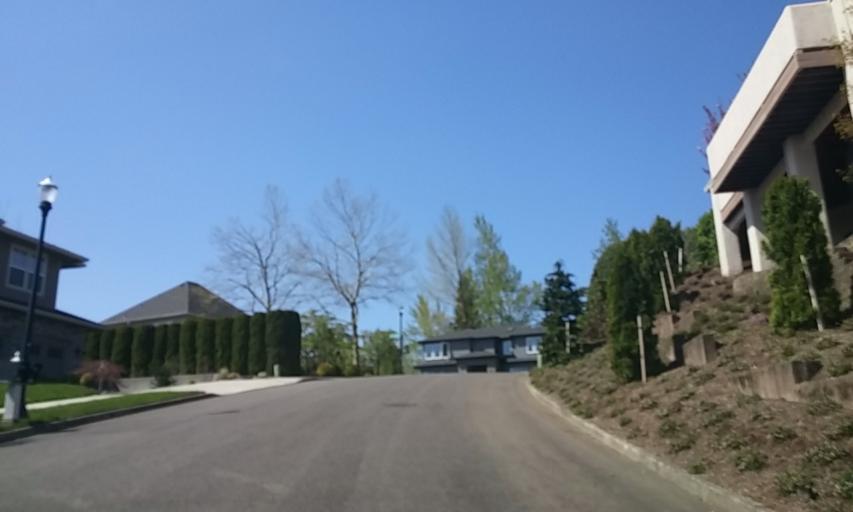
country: US
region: Oregon
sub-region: Washington County
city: West Haven
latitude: 45.5350
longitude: -122.7657
